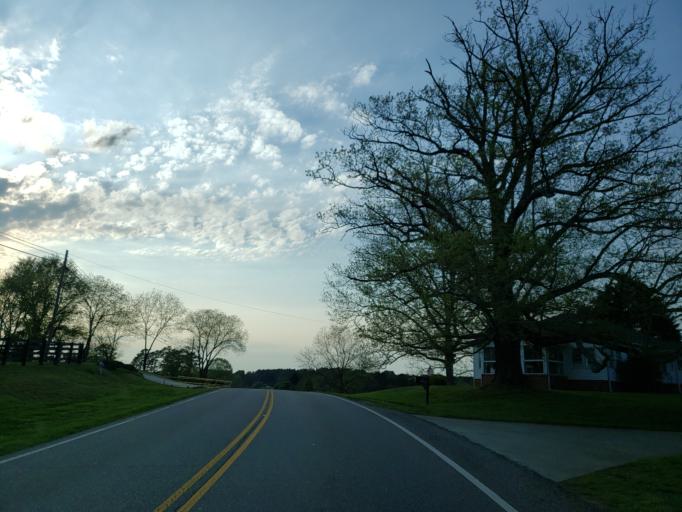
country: US
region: Georgia
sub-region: Cherokee County
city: Ball Ground
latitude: 34.2657
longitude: -84.3613
